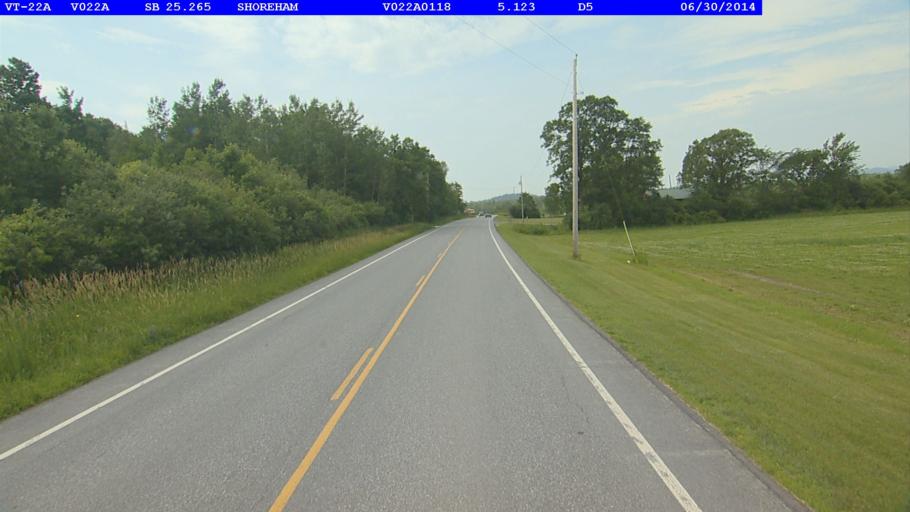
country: US
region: New York
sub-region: Essex County
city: Ticonderoga
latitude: 43.9229
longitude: -73.3116
